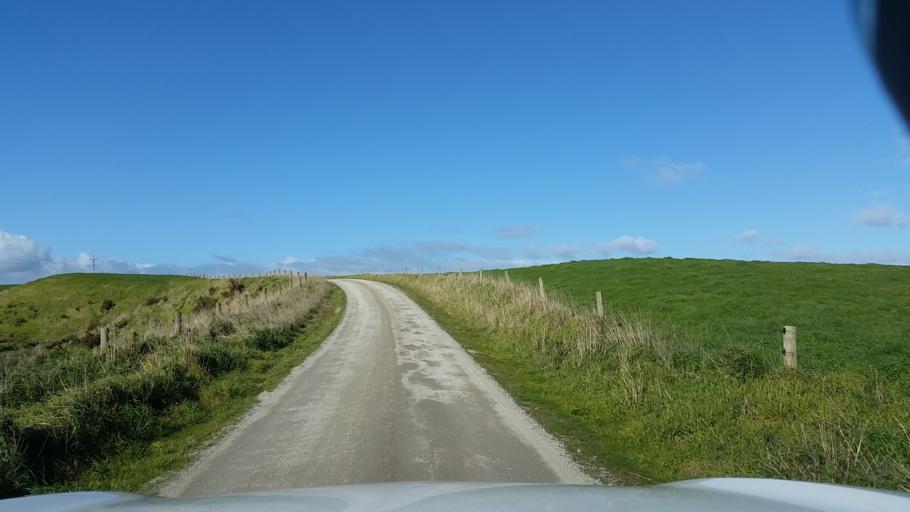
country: NZ
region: Taranaki
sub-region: South Taranaki District
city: Patea
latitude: -39.6841
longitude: 174.3918
